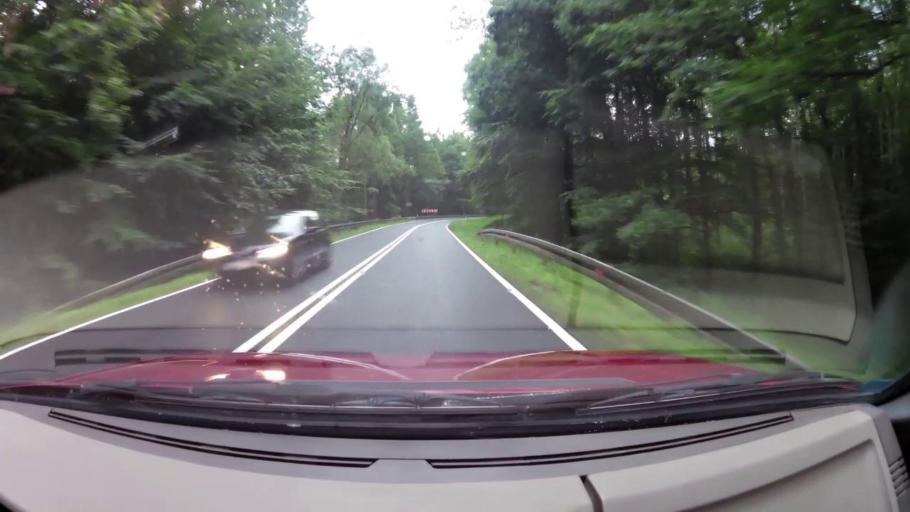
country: PL
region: West Pomeranian Voivodeship
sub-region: Powiat stargardzki
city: Chociwel
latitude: 53.4972
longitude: 15.4384
